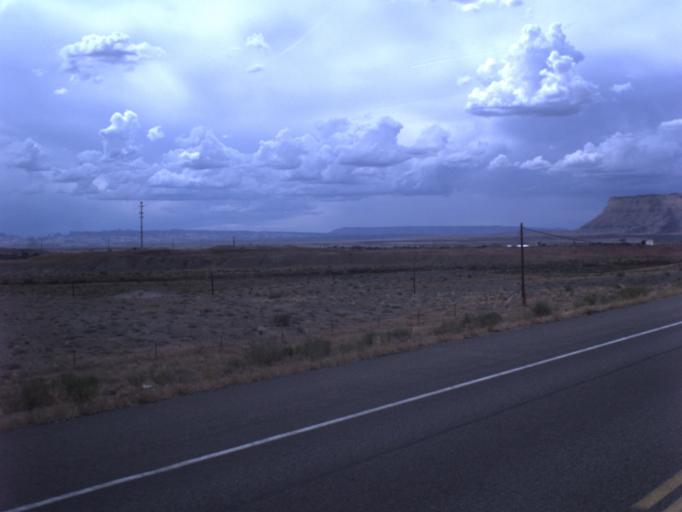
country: US
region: Utah
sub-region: Carbon County
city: East Carbon City
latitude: 38.9830
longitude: -110.1239
